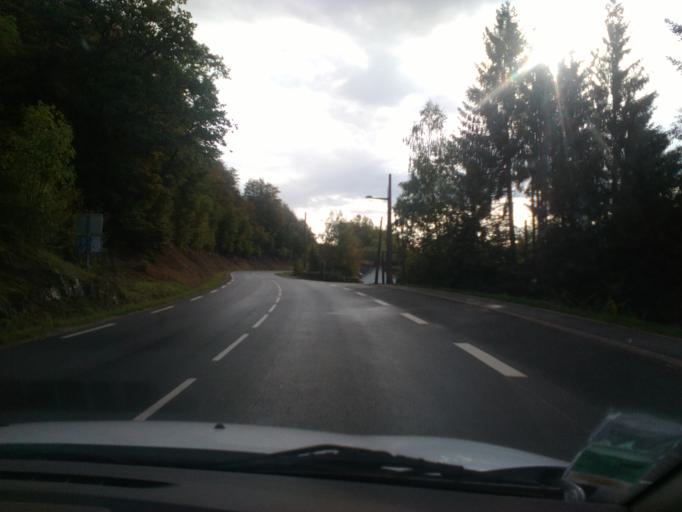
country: FR
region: Lorraine
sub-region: Departement des Vosges
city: Corcieux
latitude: 48.1669
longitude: 6.8931
